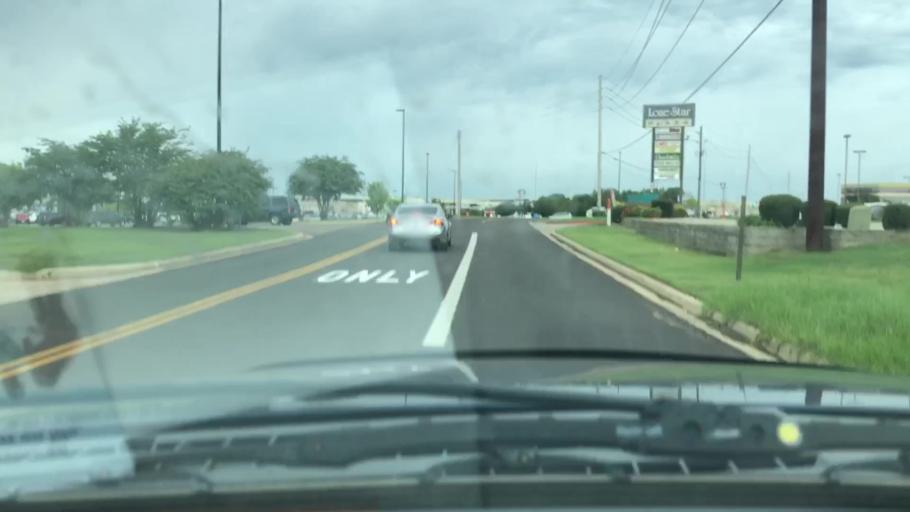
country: US
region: Texas
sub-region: Bowie County
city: Wake Village
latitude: 33.4438
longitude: -94.0993
